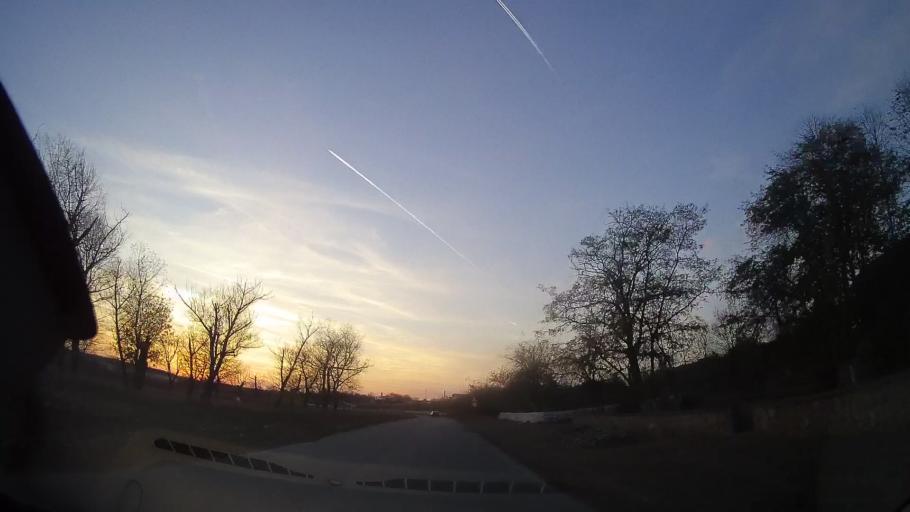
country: RO
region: Constanta
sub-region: Comuna Mereni
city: Mereni
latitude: 44.0163
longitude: 28.3221
